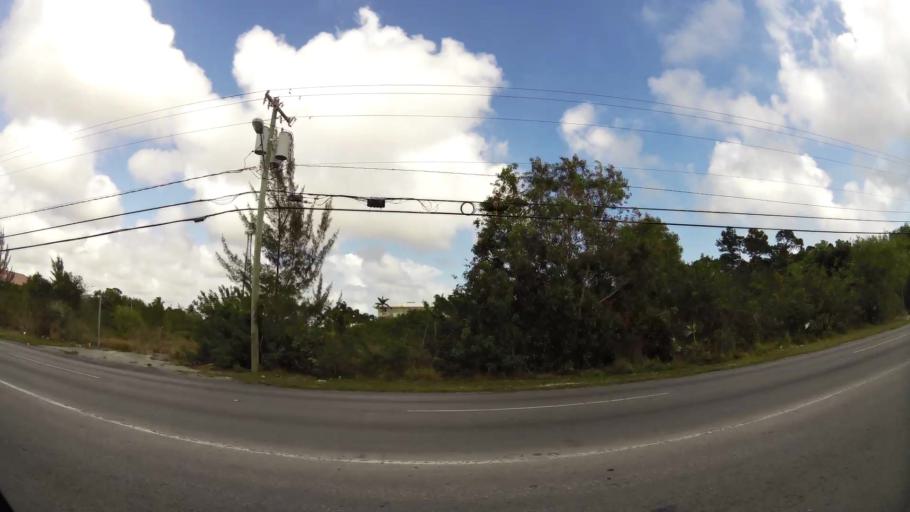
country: BS
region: Freeport
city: Freeport
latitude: 26.5289
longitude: -78.6985
